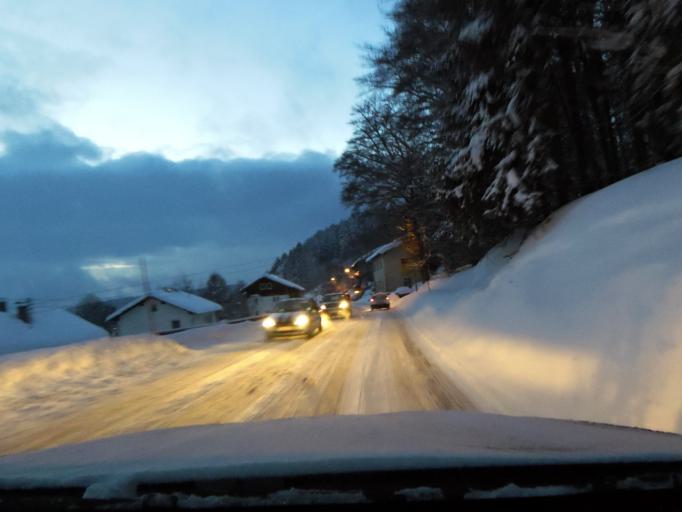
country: DE
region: Bavaria
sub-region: Lower Bavaria
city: Spiegelau
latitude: 48.9112
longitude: 13.3478
